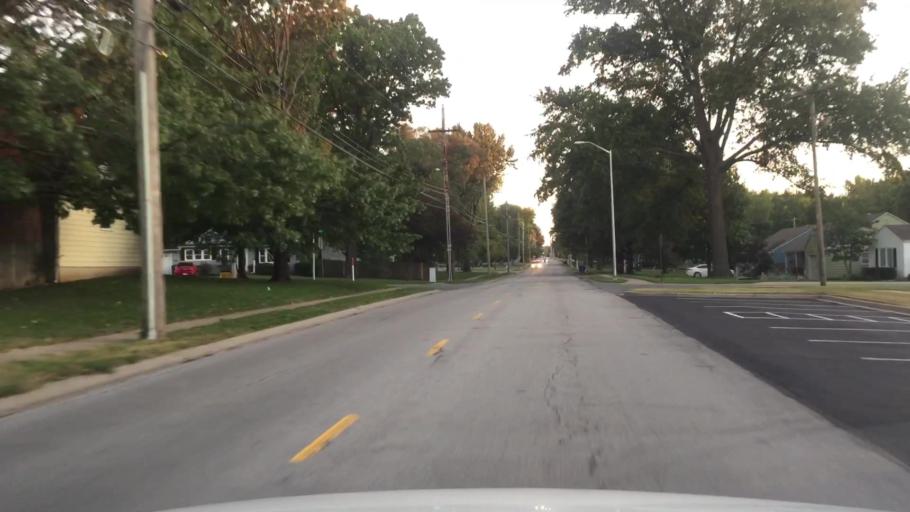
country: US
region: Kansas
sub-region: Johnson County
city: Mission
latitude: 39.0118
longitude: -94.6723
